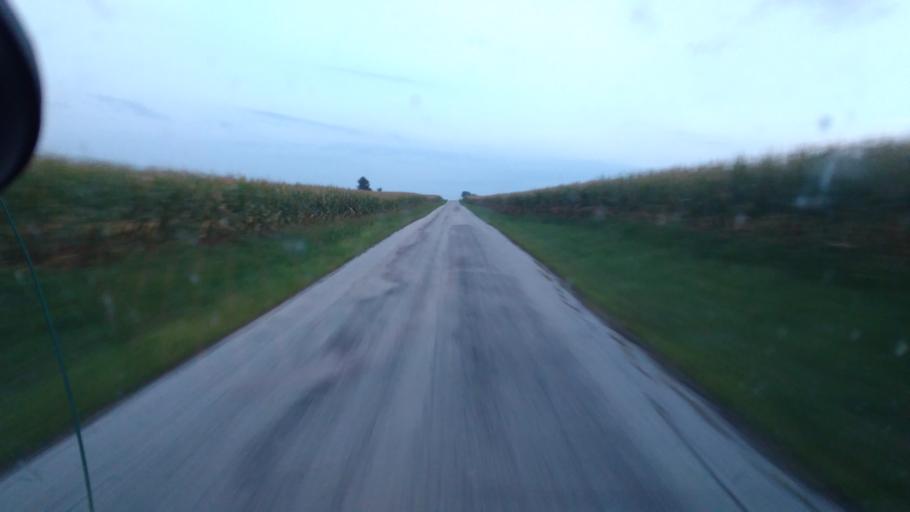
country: US
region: Ohio
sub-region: Hardin County
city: Kenton
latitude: 40.6499
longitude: -83.4584
